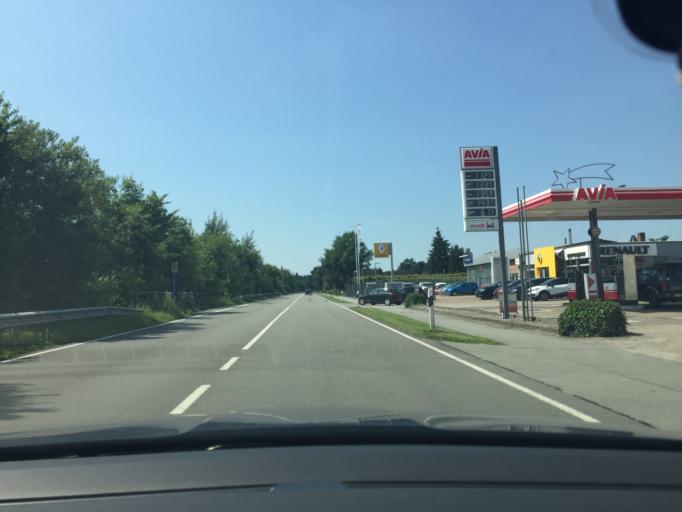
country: DE
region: Lower Saxony
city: Edewecht
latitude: 53.0936
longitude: 8.0806
